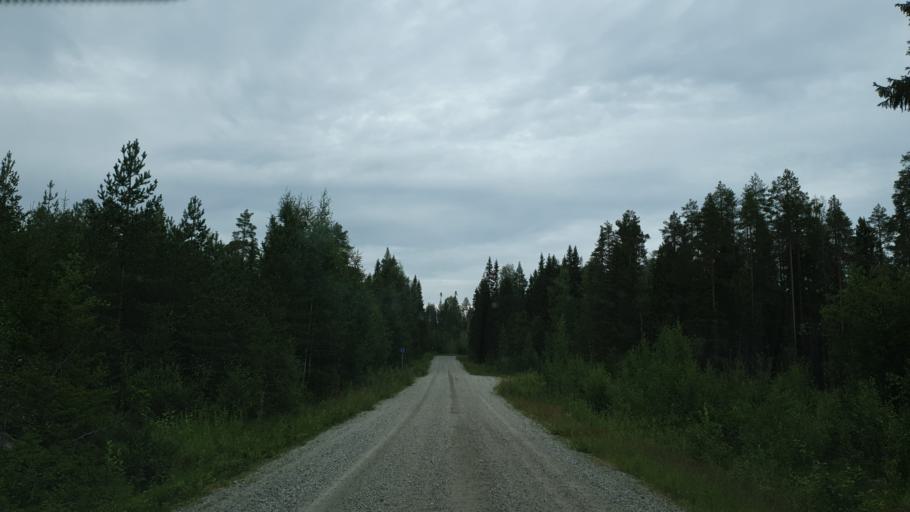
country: FI
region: Kainuu
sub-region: Kehys-Kainuu
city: Kuhmo
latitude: 64.4558
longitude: 29.5780
